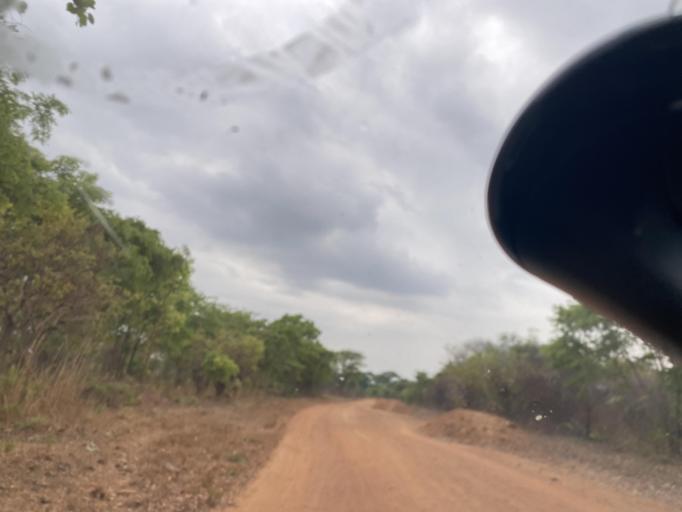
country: ZM
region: Lusaka
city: Chongwe
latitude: -15.2417
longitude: 28.7206
